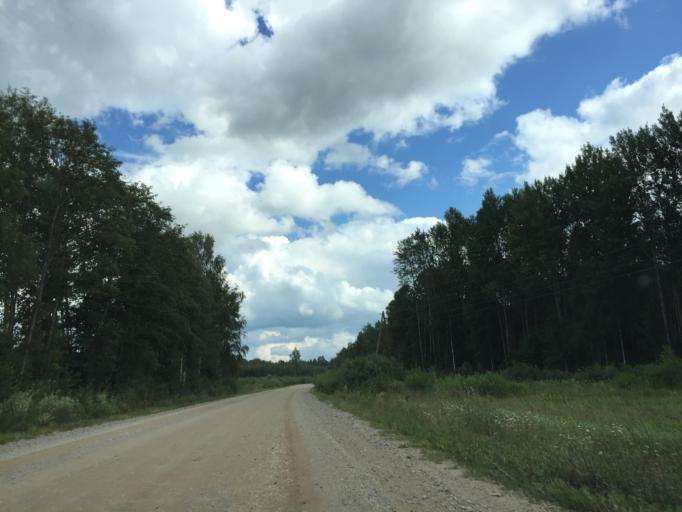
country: LV
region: Malpils
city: Malpils
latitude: 56.8792
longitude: 24.9934
